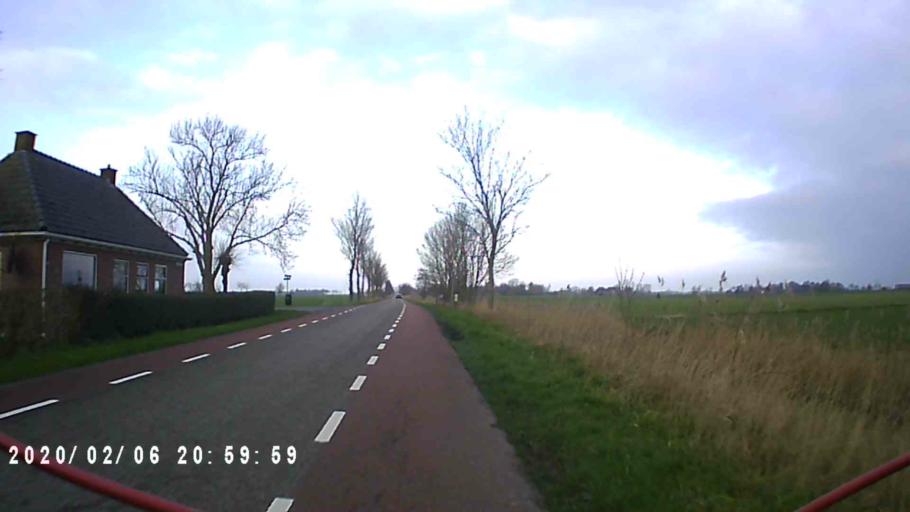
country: NL
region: Groningen
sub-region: Gemeente Zuidhorn
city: Oldehove
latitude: 53.3102
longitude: 6.4313
